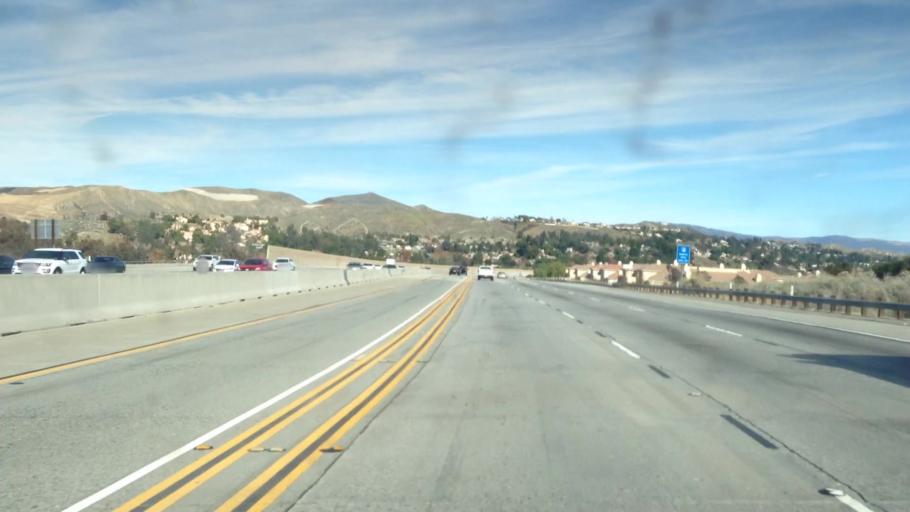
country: US
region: California
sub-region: Los Angeles County
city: Santa Clarita
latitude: 34.4089
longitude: -118.4461
